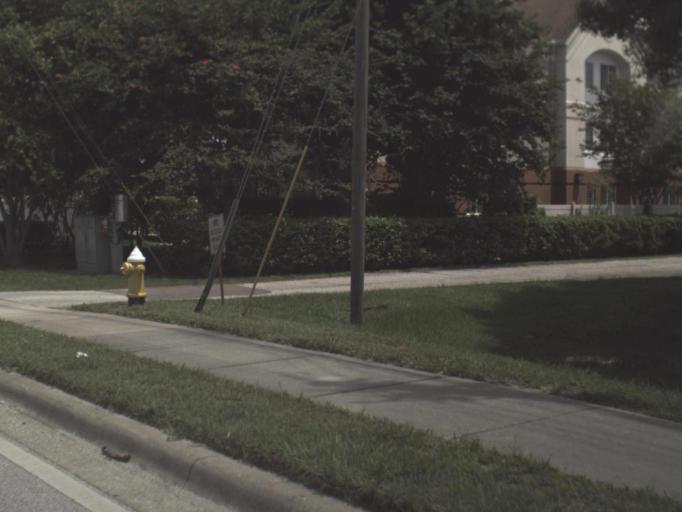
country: US
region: Florida
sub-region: Pinellas County
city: South Highpoint
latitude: 27.8917
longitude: -82.7002
